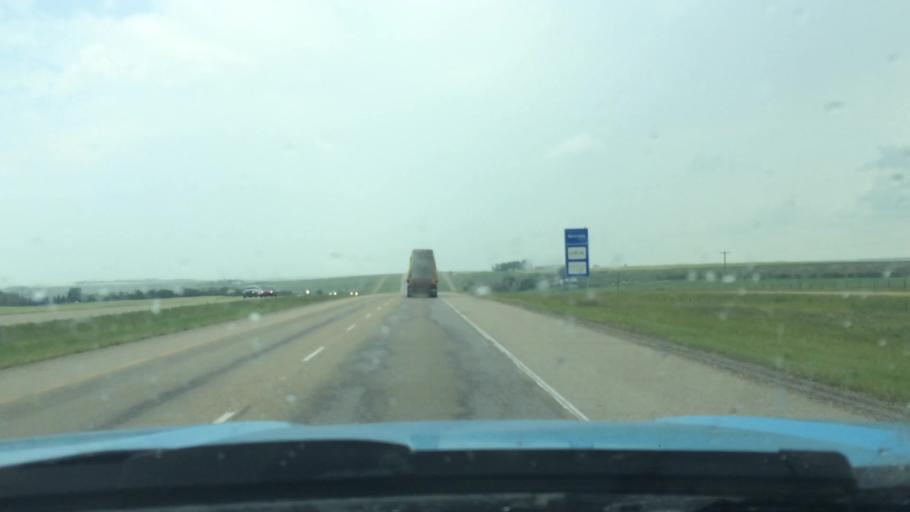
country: CA
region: Alberta
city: Carstairs
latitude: 51.5406
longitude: -114.0250
